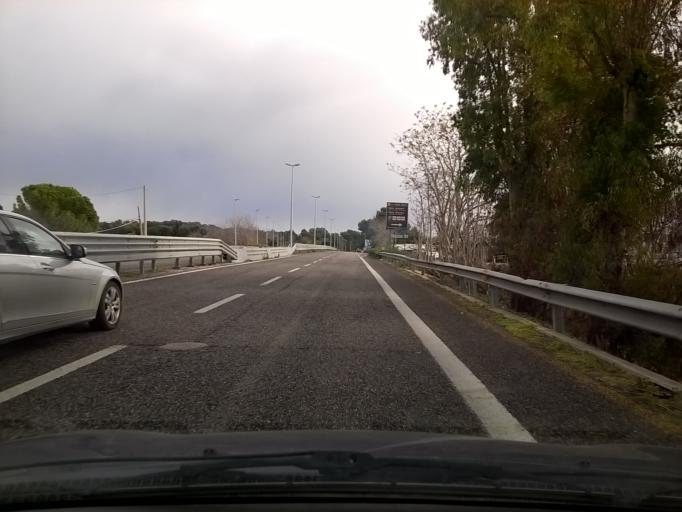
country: IT
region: Apulia
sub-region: Provincia di Taranto
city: Paolo VI
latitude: 40.4668
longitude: 17.2814
